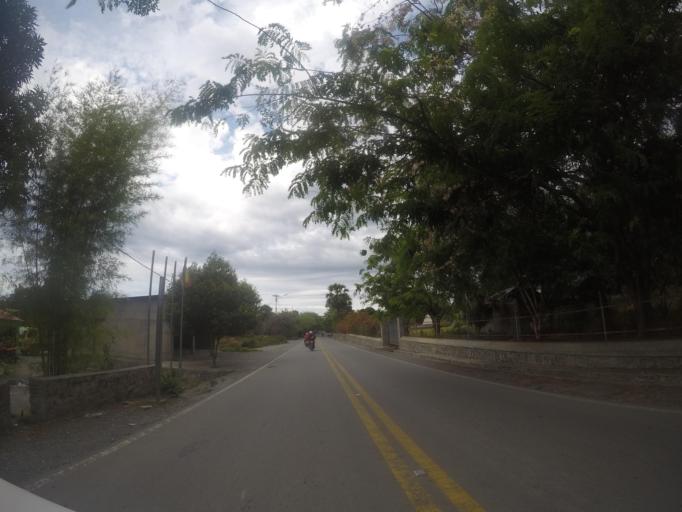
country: TL
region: Liquica
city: Liquica
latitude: -8.5913
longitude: 125.3295
